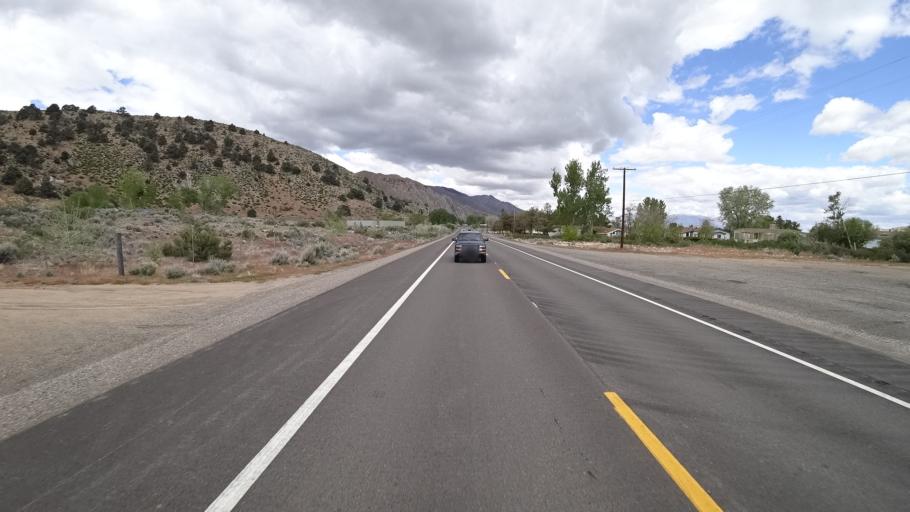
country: US
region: Nevada
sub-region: Lyon County
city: Smith Valley
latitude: 38.5314
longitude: -119.4906
